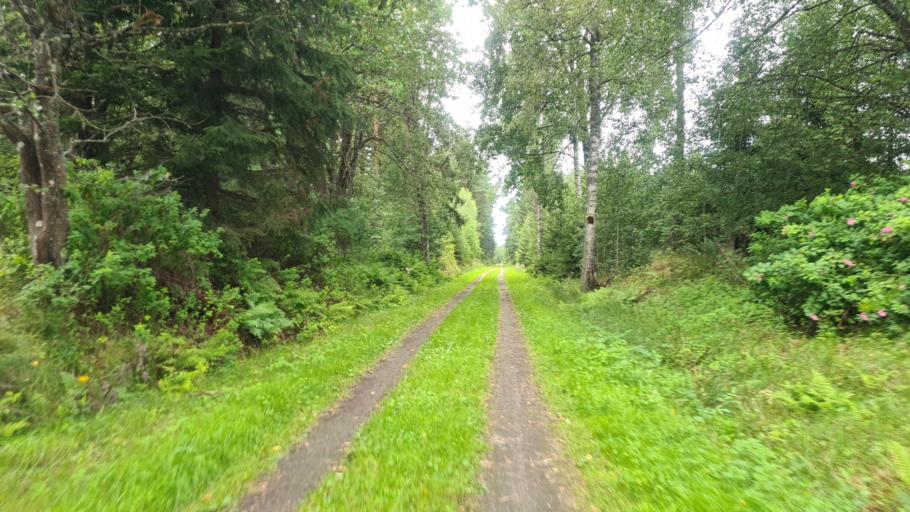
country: SE
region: Kronoberg
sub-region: Ljungby Kommun
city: Ljungby
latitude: 56.8261
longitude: 13.8878
